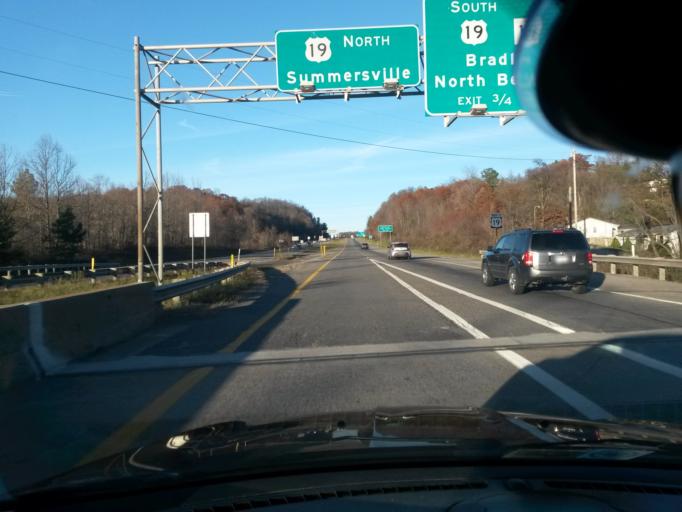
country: US
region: West Virginia
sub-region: Raleigh County
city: Prosperity
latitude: 37.8398
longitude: -81.2121
